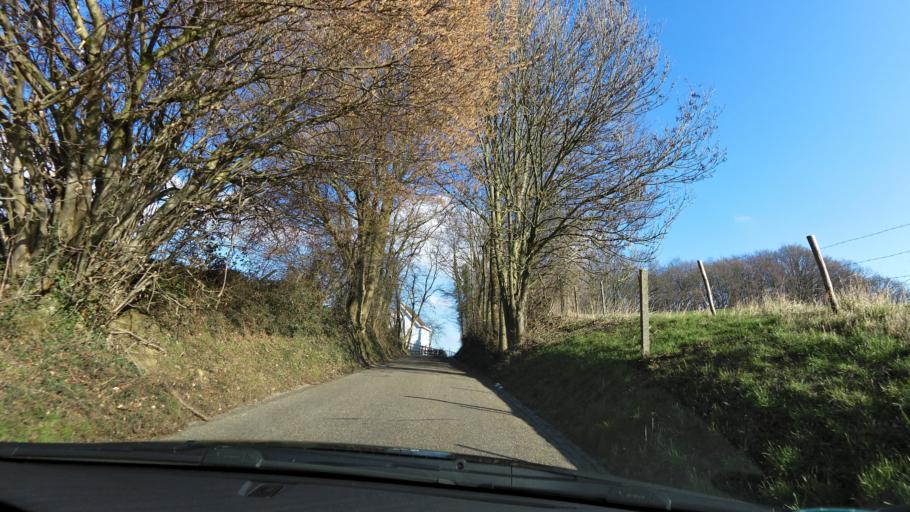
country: NL
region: Limburg
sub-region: Gemeente Nuth
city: Nuth
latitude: 50.9245
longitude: 5.9009
